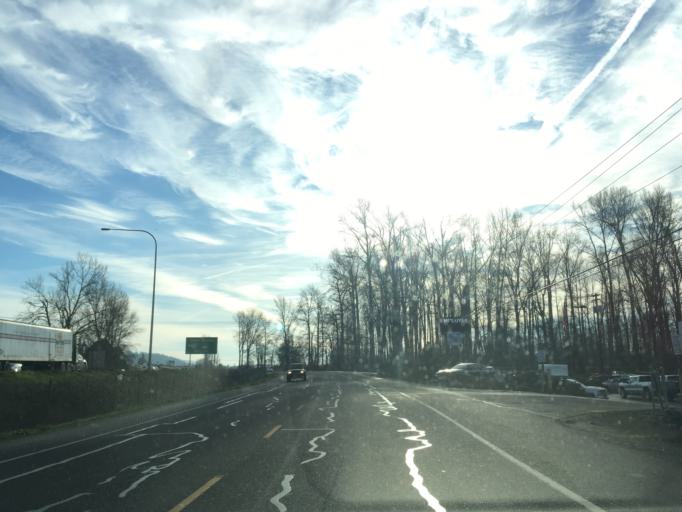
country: US
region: Washington
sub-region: Skagit County
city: Mount Vernon
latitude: 48.4316
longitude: -122.3416
